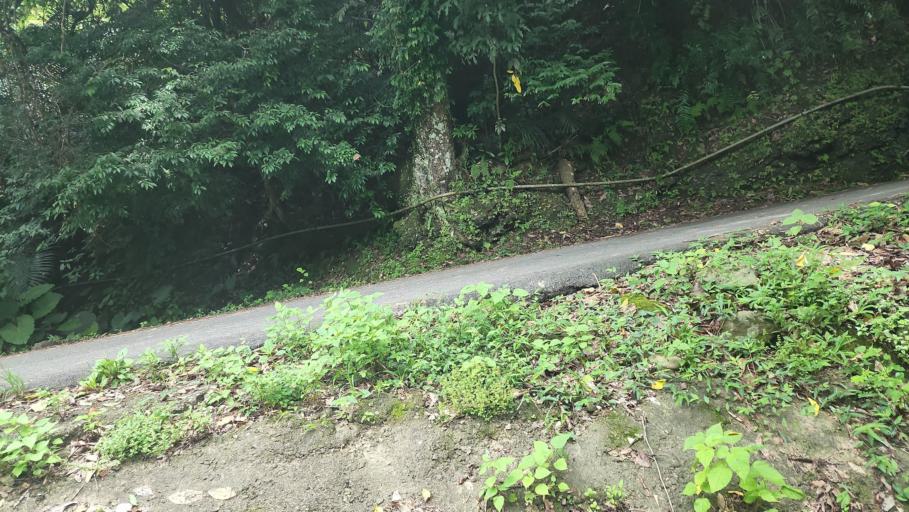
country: TW
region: Taiwan
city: Daxi
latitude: 24.8722
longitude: 121.3852
